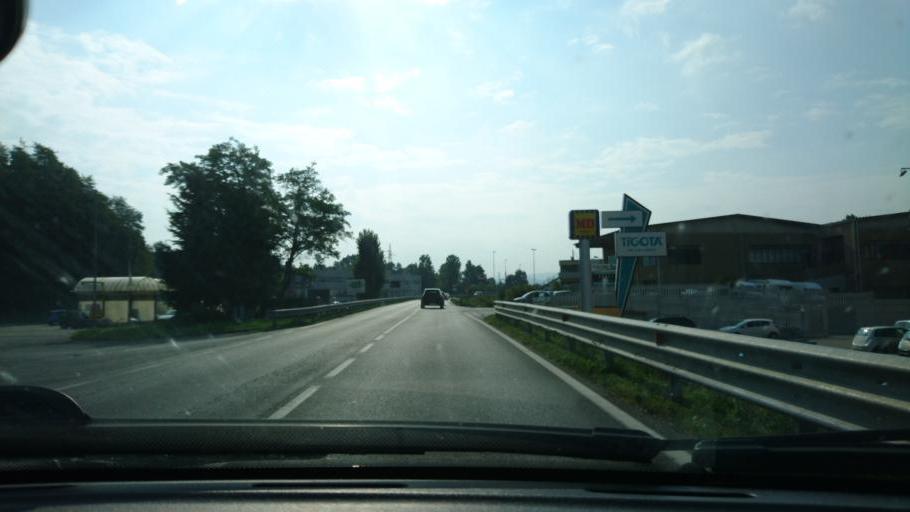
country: IT
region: Liguria
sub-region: Provincia di Savona
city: Cairo Montenotte
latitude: 44.3873
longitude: 8.2822
